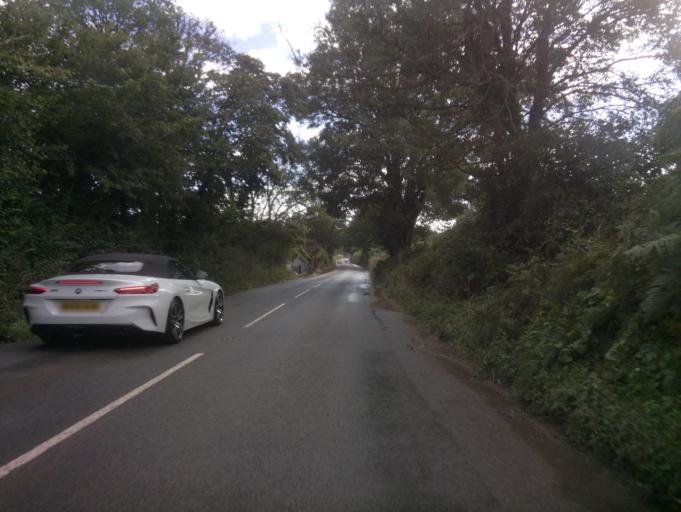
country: GB
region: England
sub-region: Devon
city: Ivybridge
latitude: 50.3555
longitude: -3.9243
